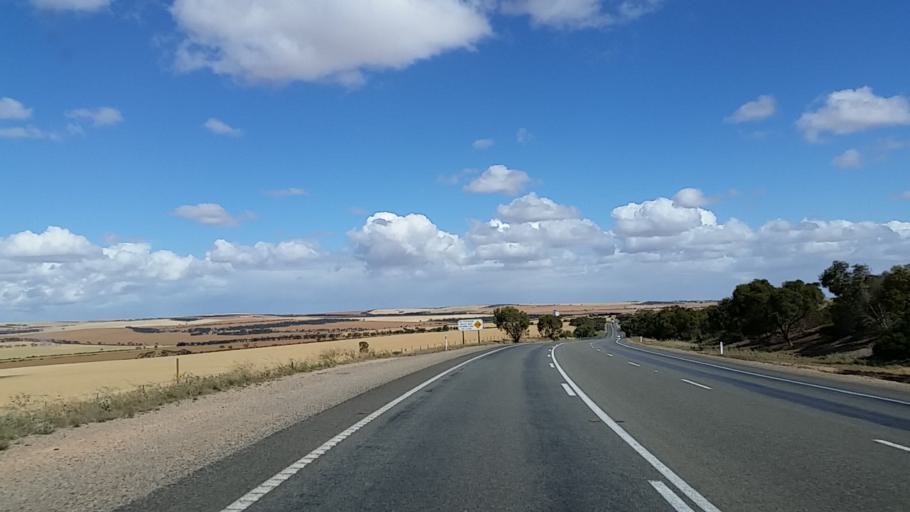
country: AU
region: South Australia
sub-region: Wakefield
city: Balaklava
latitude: -33.9803
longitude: 138.2057
